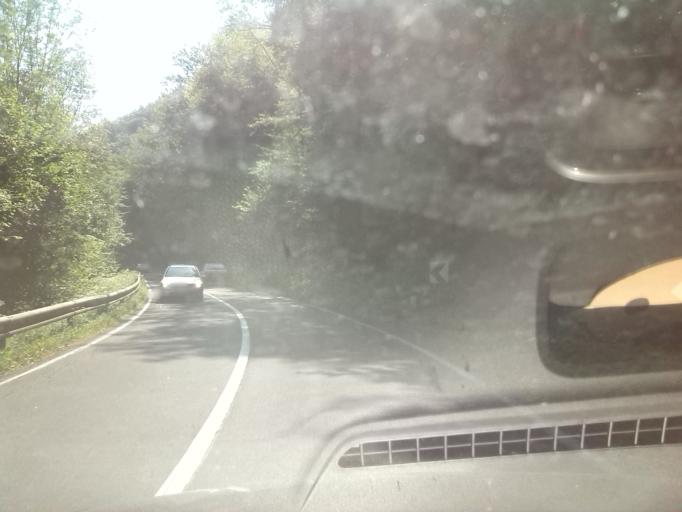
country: IT
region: Friuli Venezia Giulia
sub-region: Provincia di Udine
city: Cras
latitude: 46.2039
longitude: 13.6522
